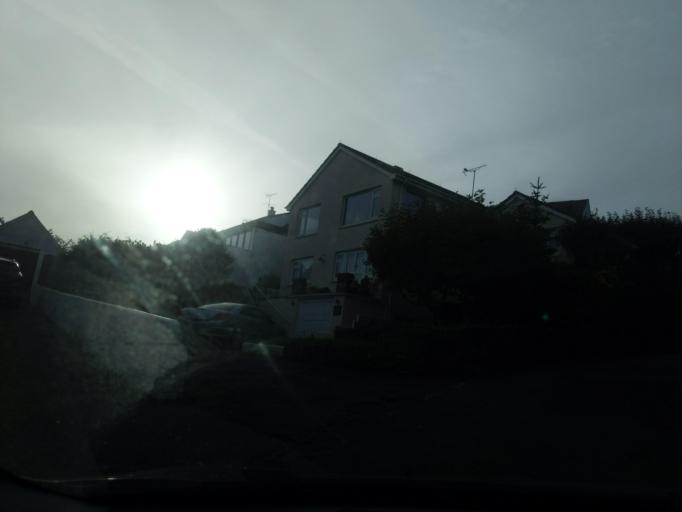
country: GB
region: England
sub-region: Cornwall
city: Looe
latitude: 50.3582
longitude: -4.4462
